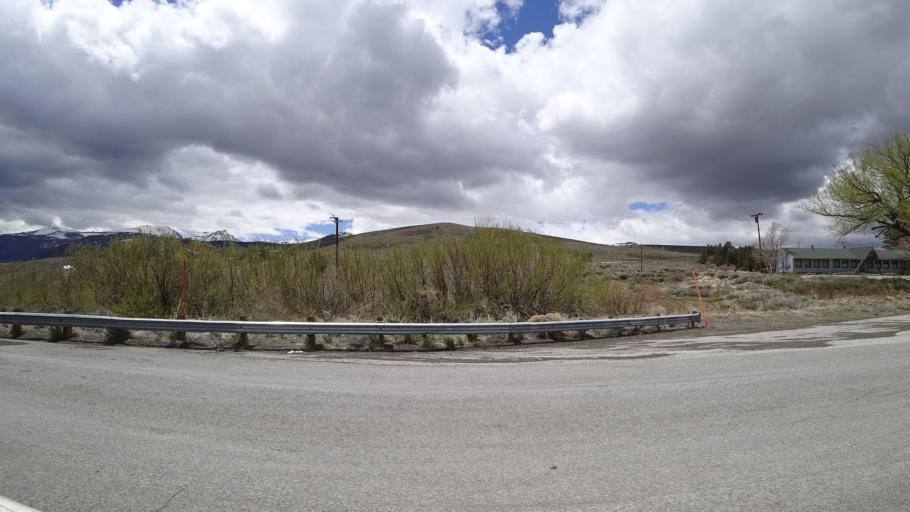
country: US
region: California
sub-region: Mono County
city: Bridgeport
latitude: 38.0869
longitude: -119.1821
